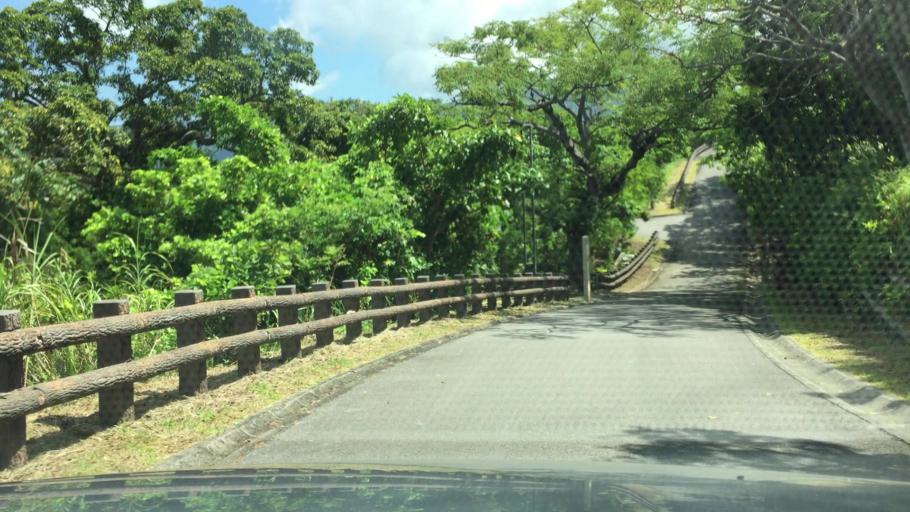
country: JP
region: Okinawa
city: Ishigaki
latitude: 24.3846
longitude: 124.1616
